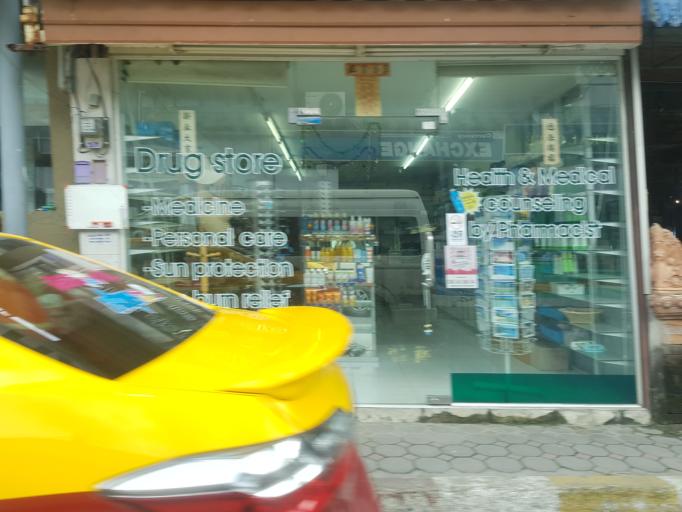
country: TH
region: Surat Thani
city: Ko Samui
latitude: 9.4633
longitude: 100.0434
